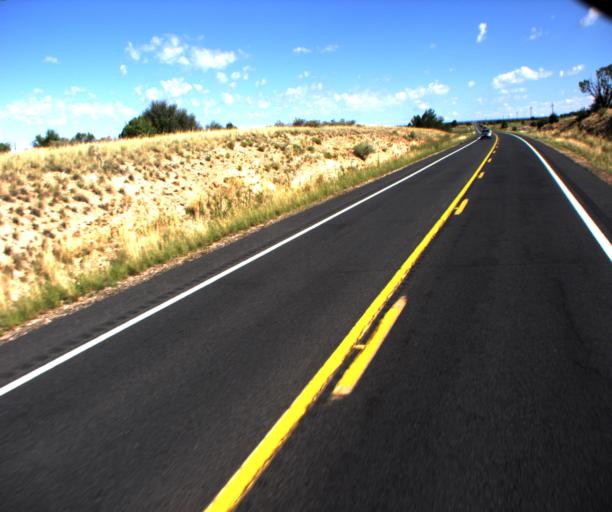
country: US
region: Arizona
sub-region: Coconino County
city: Grand Canyon Village
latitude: 35.7120
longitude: -112.1313
